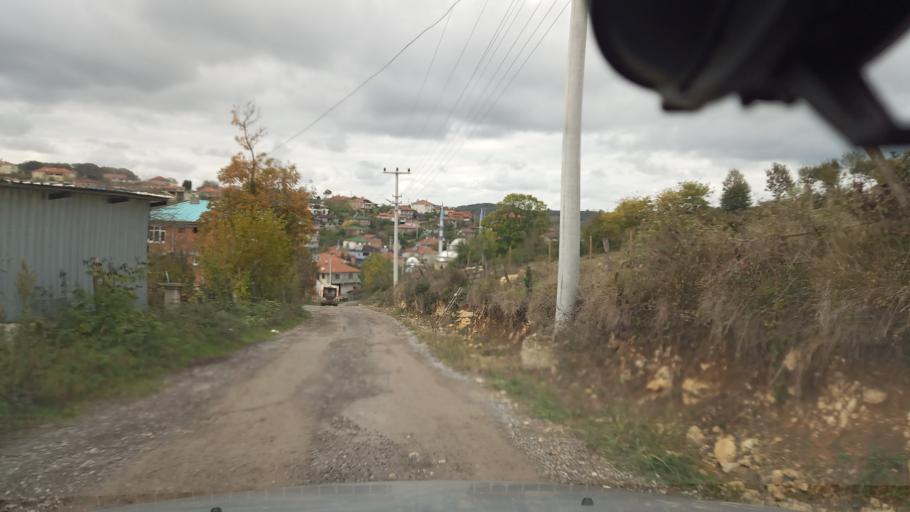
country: TR
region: Sakarya
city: Karasu
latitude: 41.0917
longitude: 30.5850
